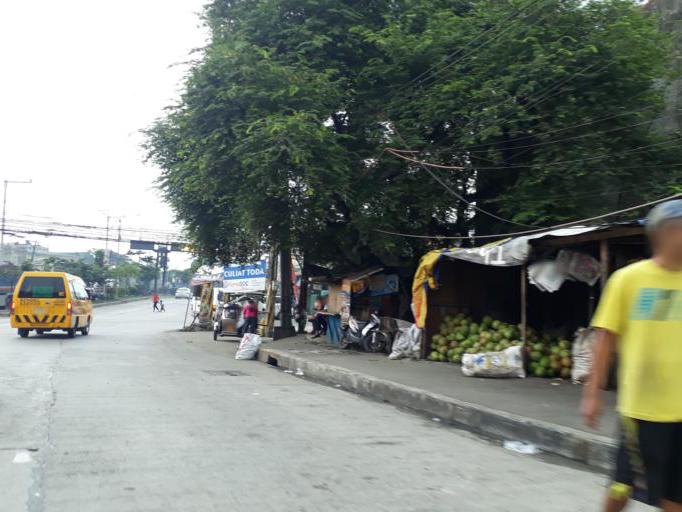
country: PH
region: Calabarzon
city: Bagong Pagasa
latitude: 14.6732
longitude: 121.0488
